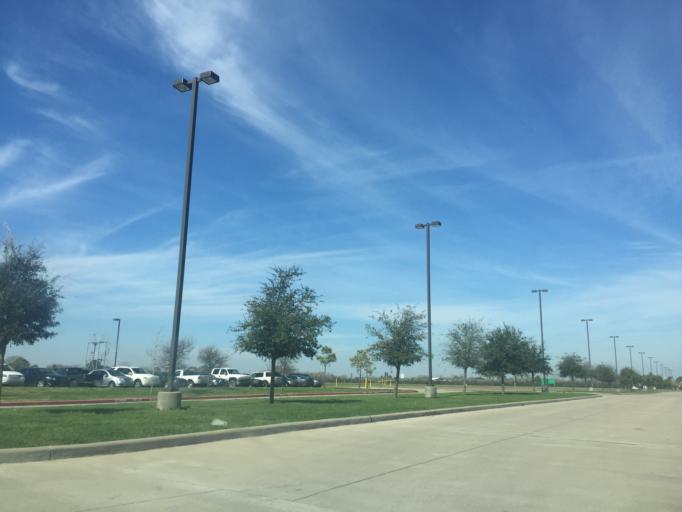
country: US
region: Texas
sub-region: Galveston County
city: Kemah
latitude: 29.5106
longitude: -95.0253
